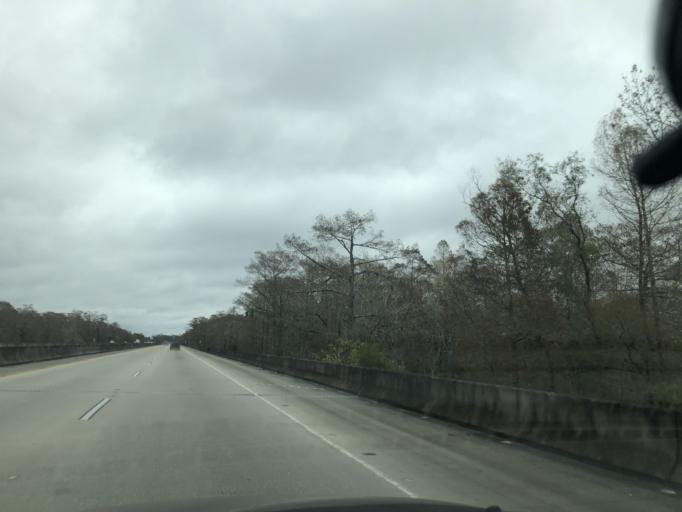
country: US
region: Louisiana
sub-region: Saint Charles Parish
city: Destrehan
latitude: 29.9645
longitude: -90.3485
